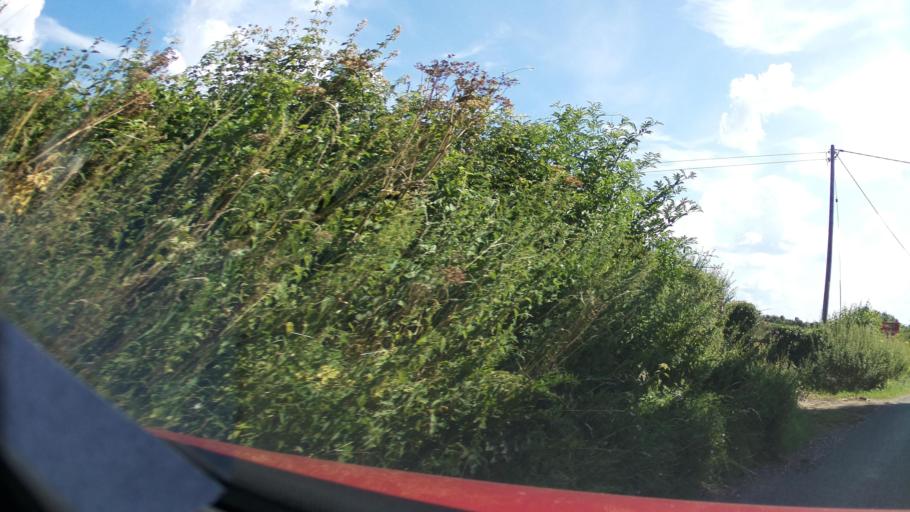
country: GB
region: England
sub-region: West Berkshire
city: Farnborough
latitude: 51.4910
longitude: -1.3656
